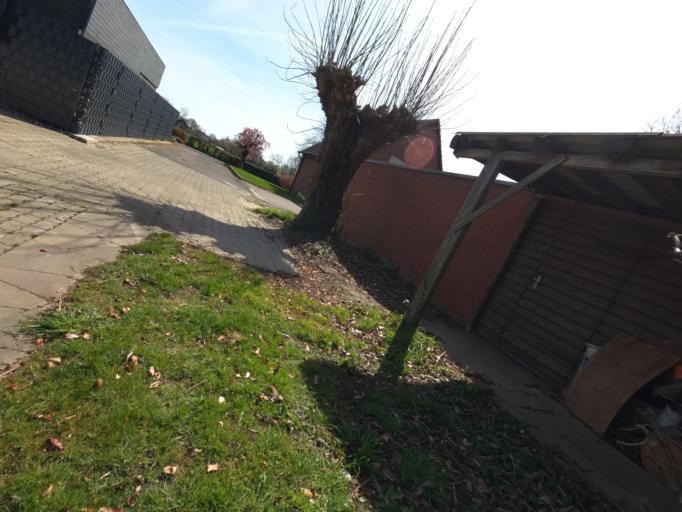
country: DE
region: North Rhine-Westphalia
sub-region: Regierungsbezirk Koln
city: Ubach-Palenberg
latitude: 50.9461
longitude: 6.1532
